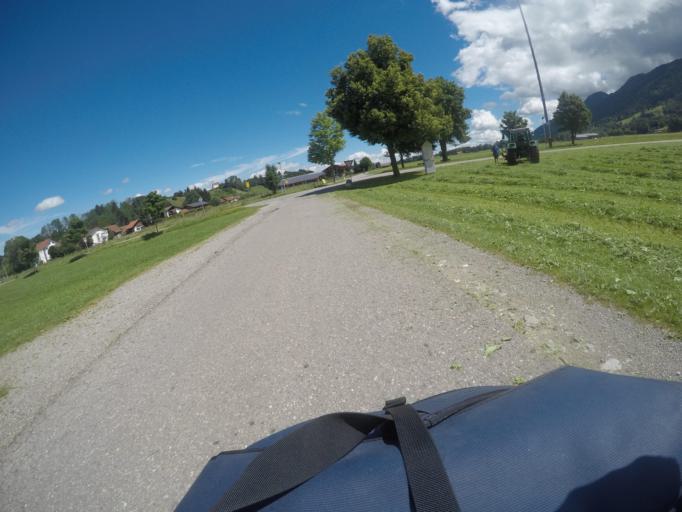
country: DE
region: Bavaria
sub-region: Swabia
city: Halblech
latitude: 47.6235
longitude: 10.8035
